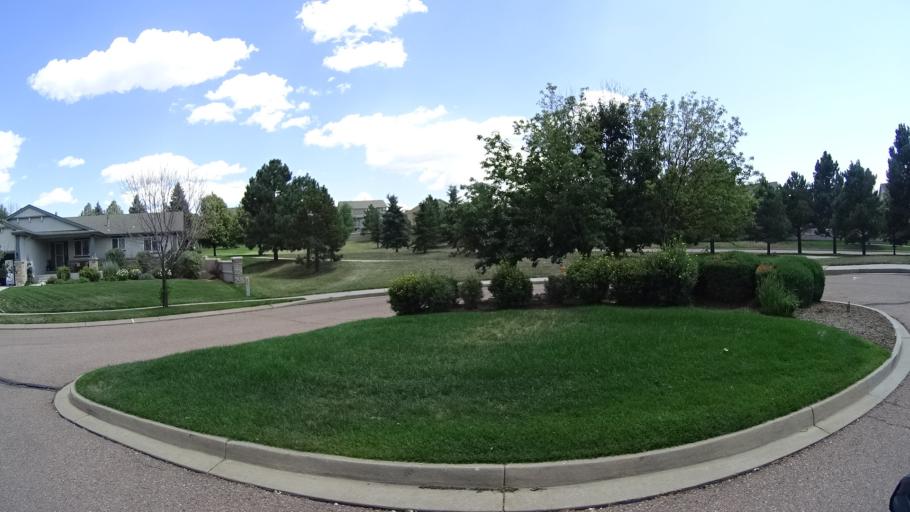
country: US
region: Colorado
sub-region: El Paso County
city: Black Forest
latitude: 38.9688
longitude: -104.7649
